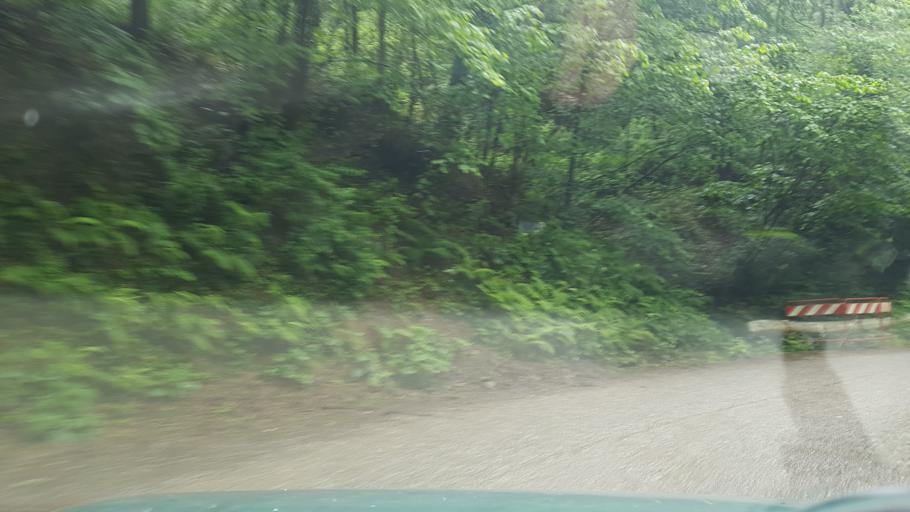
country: IT
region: Friuli Venezia Giulia
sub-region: Provincia di Gorizia
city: San Floriano del Collio
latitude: 45.9546
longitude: 13.5976
